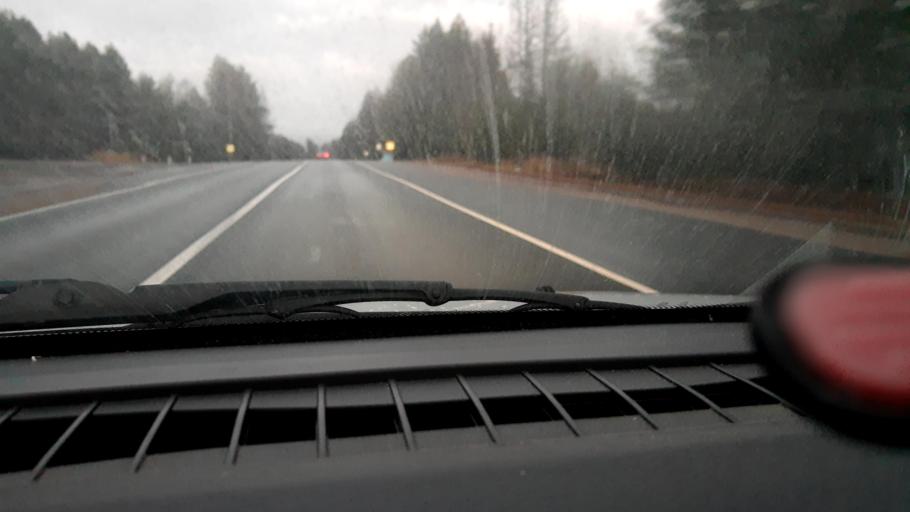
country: RU
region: Nizjnij Novgorod
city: Uren'
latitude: 57.2949
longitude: 45.6548
